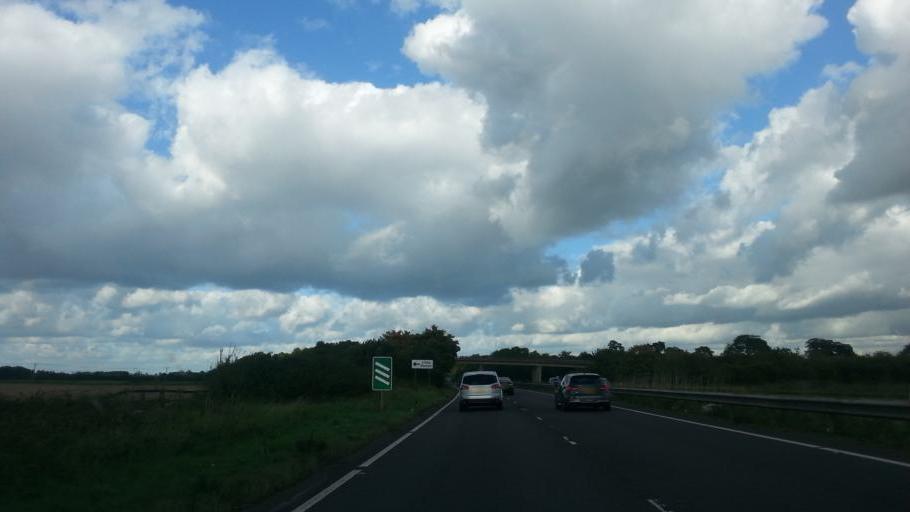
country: GB
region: England
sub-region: Cambridgeshire
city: Little Paxton
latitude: 52.2504
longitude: -0.2683
